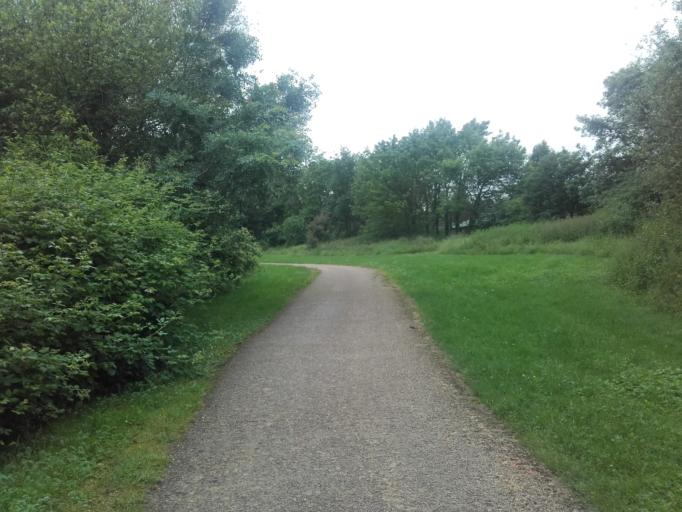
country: FR
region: Centre
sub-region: Departement d'Indre-et-Loire
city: Joue-les-Tours
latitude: 47.3624
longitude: 0.6811
